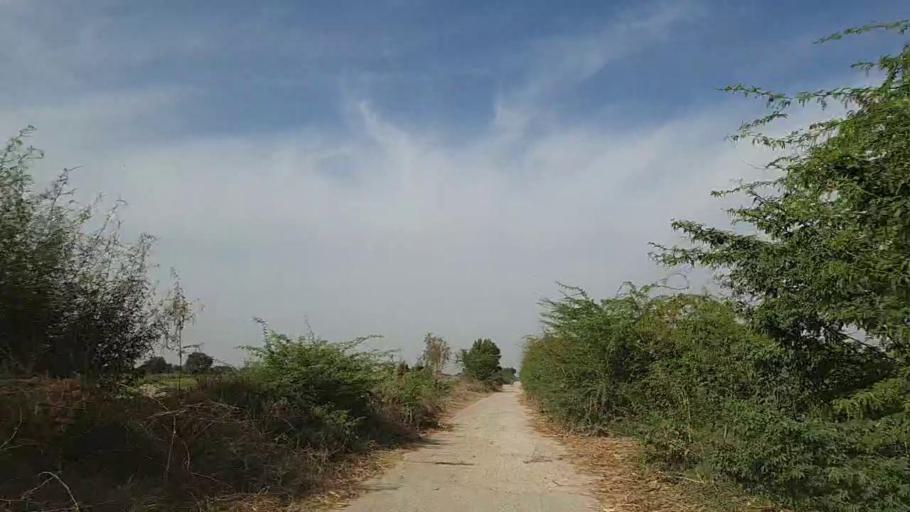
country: PK
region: Sindh
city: Samaro
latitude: 25.2351
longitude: 69.4240
